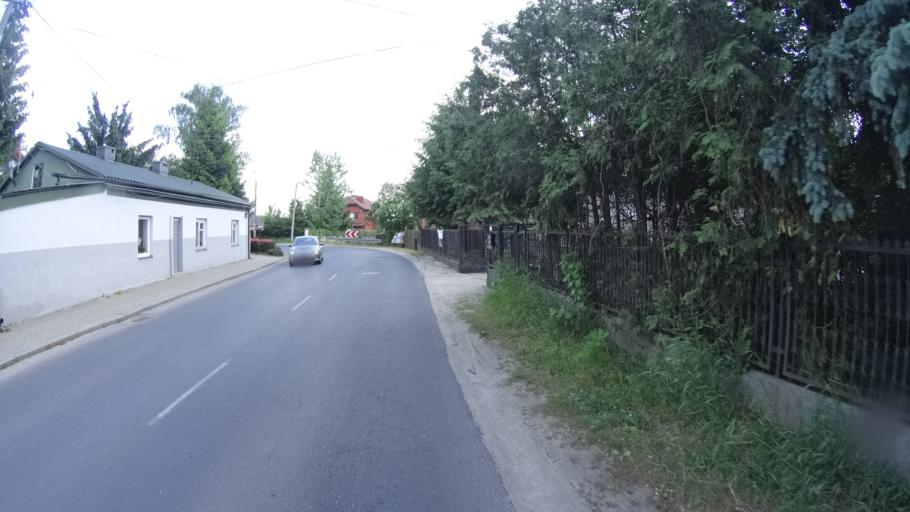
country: PL
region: Masovian Voivodeship
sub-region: Powiat piaseczynski
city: Tarczyn
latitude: 51.9816
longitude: 20.8308
